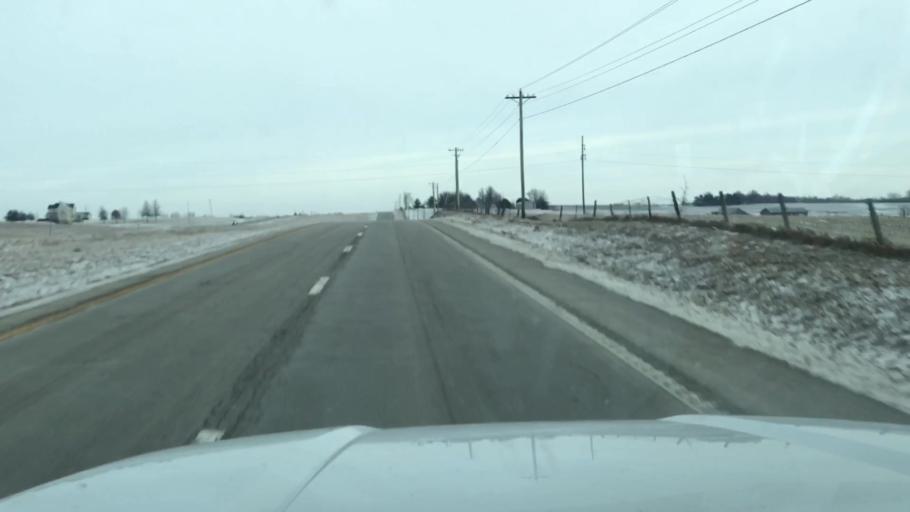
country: US
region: Missouri
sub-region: Andrew County
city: Savannah
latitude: 39.9868
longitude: -94.8800
